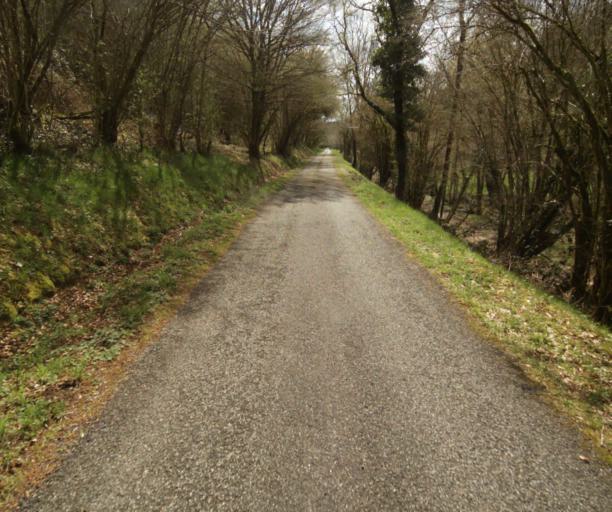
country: FR
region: Limousin
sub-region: Departement de la Correze
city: Argentat
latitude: 45.1825
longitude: 1.8767
